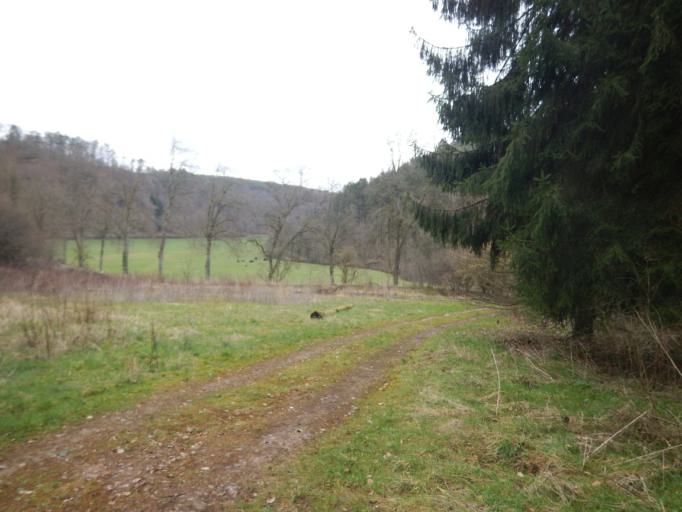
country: LU
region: Luxembourg
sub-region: Canton de Mersch
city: Tuntange
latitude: 49.7128
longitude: 6.0543
